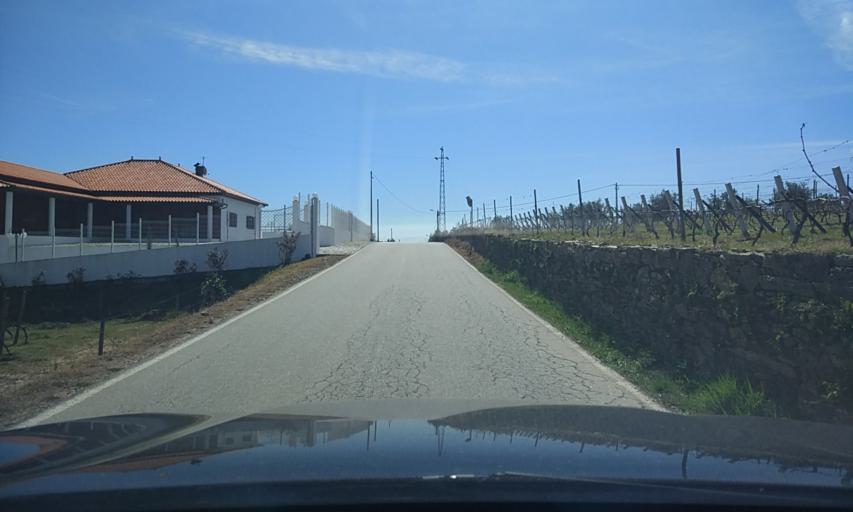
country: PT
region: Vila Real
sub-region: Sabrosa
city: Sabrosa
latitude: 41.3121
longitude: -7.5605
